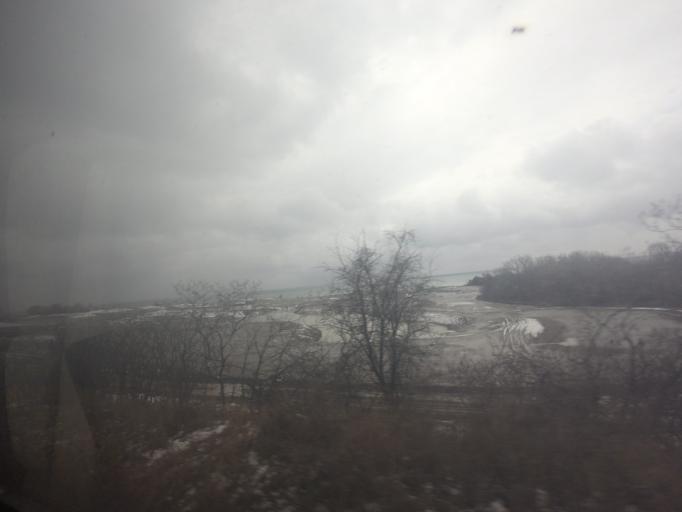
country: CA
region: Ontario
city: Cobourg
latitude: 43.9419
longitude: -78.3228
